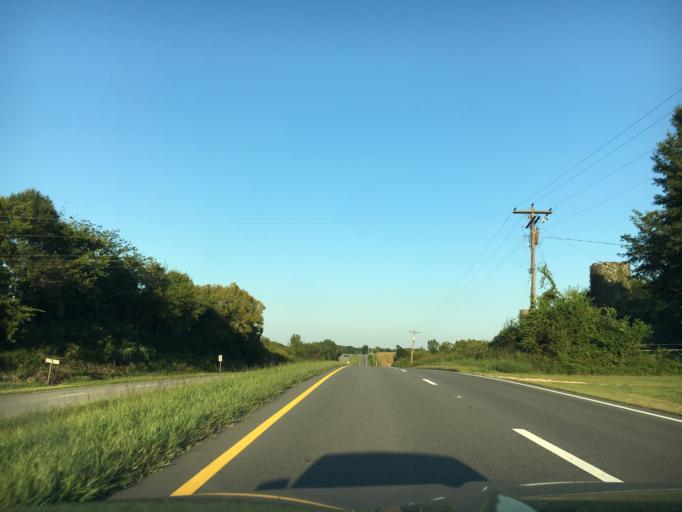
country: US
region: Virginia
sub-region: City of Danville
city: Danville
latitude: 36.5809
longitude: -79.1929
